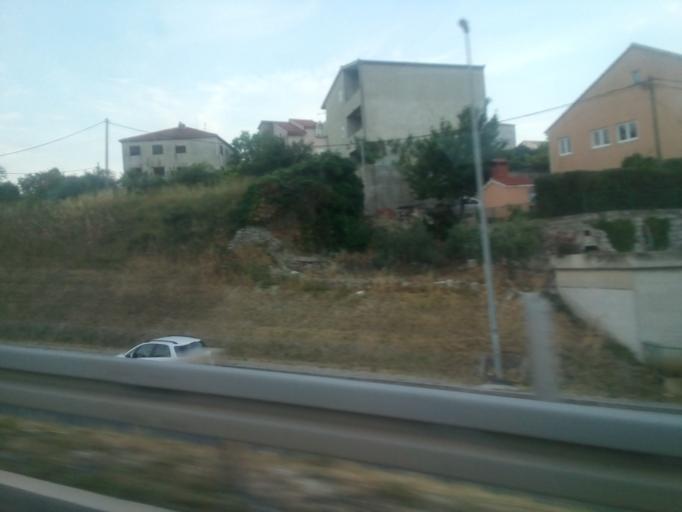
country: HR
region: Splitsko-Dalmatinska
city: Vranjic
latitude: 43.5140
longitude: 16.4828
